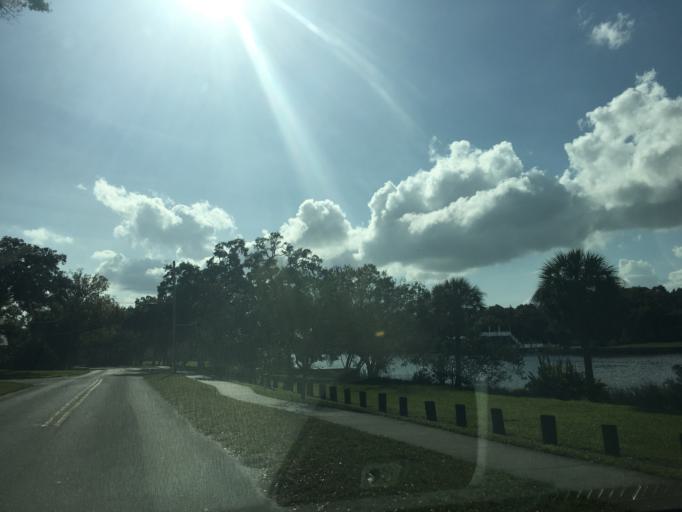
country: US
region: Florida
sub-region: Hillsborough County
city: Tampa
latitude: 27.9942
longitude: -82.4648
